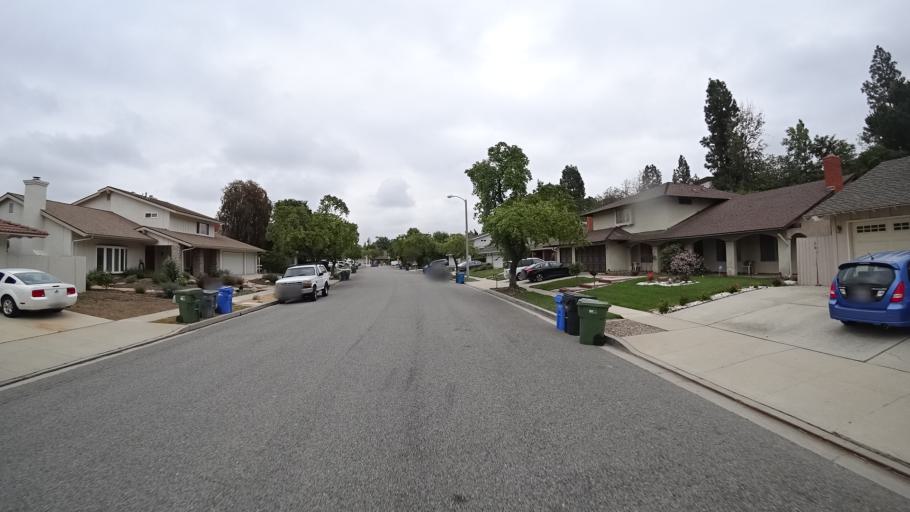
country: US
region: California
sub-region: Ventura County
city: Thousand Oaks
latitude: 34.2092
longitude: -118.8825
